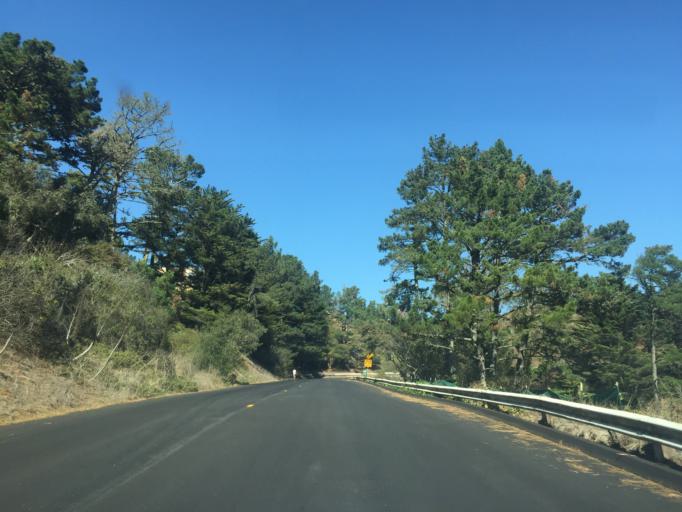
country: US
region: California
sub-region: San Francisco County
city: San Francisco
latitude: 37.7485
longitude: -122.4484
